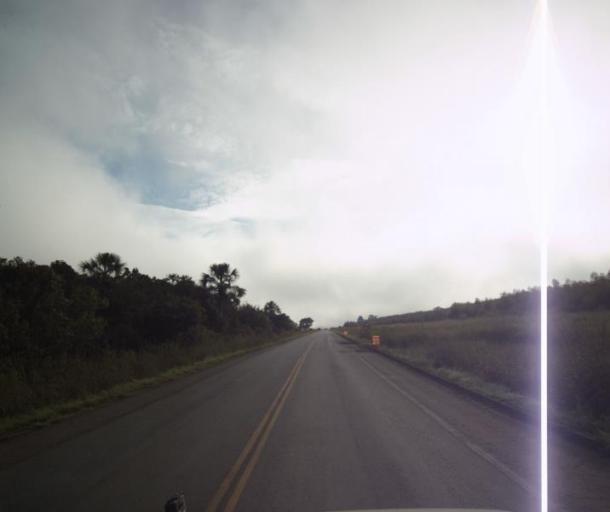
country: BR
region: Goias
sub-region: Pirenopolis
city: Pirenopolis
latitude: -15.7598
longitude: -48.7552
